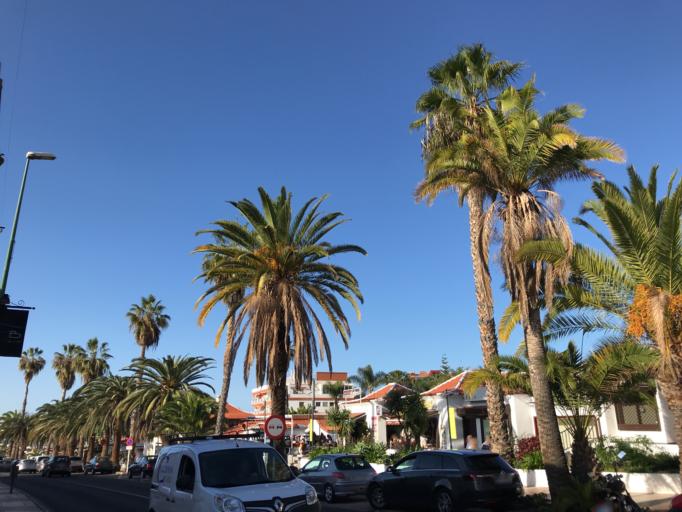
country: ES
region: Canary Islands
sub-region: Provincia de Santa Cruz de Tenerife
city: Puerto de la Cruz
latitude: 28.4130
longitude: -16.5380
